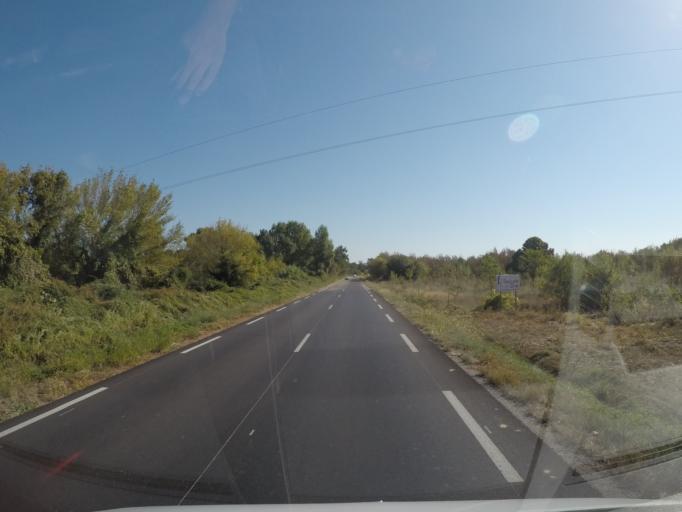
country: FR
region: Languedoc-Roussillon
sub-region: Departement du Gard
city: Lezan
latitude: 44.0236
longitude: 4.0640
